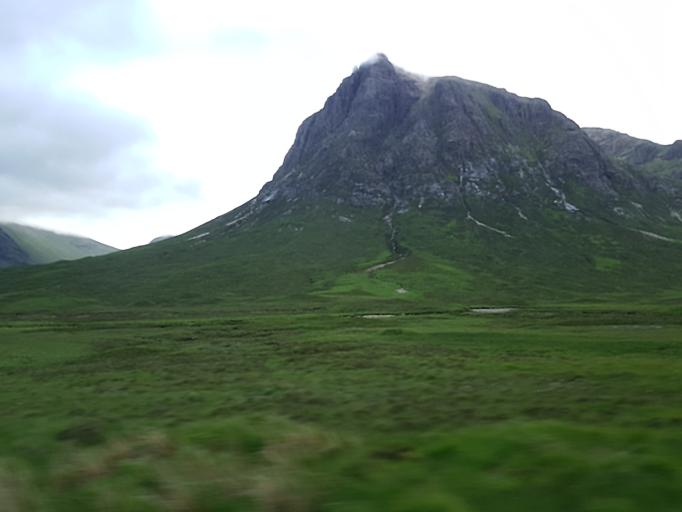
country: GB
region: Scotland
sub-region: Highland
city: Spean Bridge
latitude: 56.6594
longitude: -4.8843
